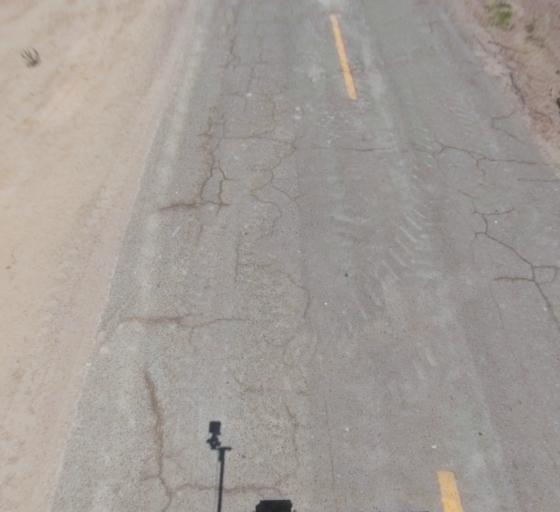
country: US
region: California
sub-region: Madera County
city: Parkwood
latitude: 36.8658
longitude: -120.1605
